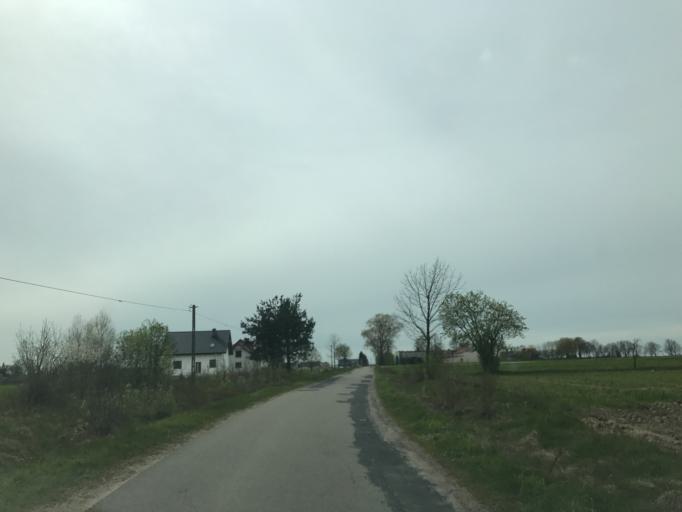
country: PL
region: Warmian-Masurian Voivodeship
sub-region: Powiat dzialdowski
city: Lidzbark
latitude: 53.3482
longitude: 19.8294
